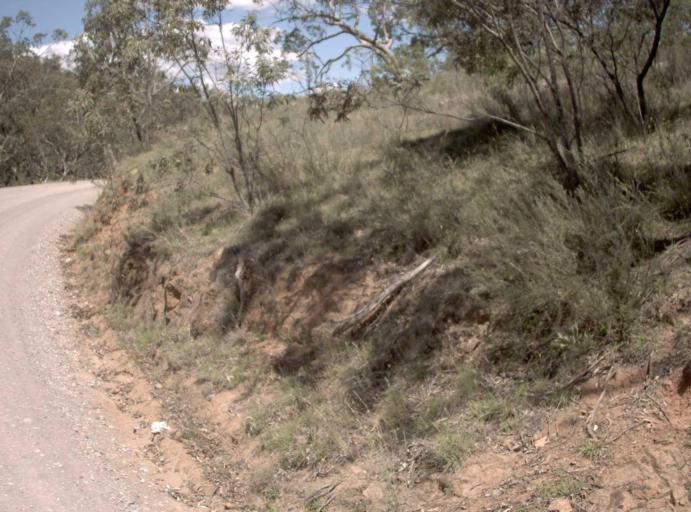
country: AU
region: New South Wales
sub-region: Snowy River
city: Jindabyne
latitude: -37.0516
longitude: 148.5658
